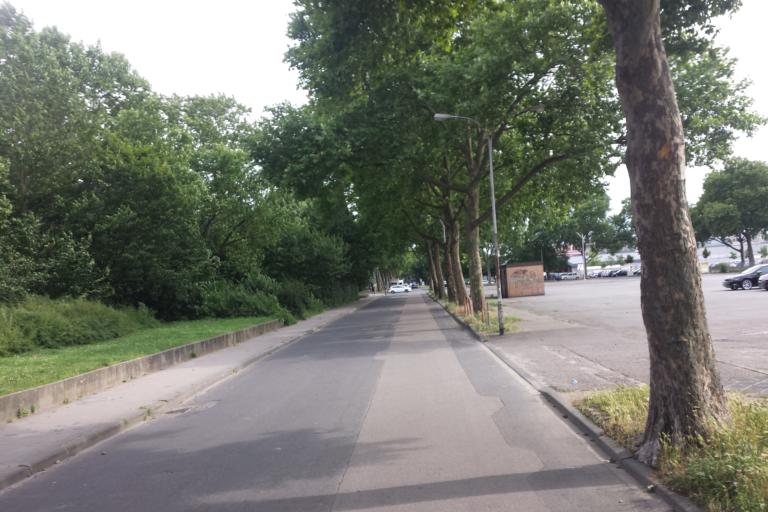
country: DE
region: Baden-Wuerttemberg
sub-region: Karlsruhe Region
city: Mannheim
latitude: 49.5051
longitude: 8.4773
